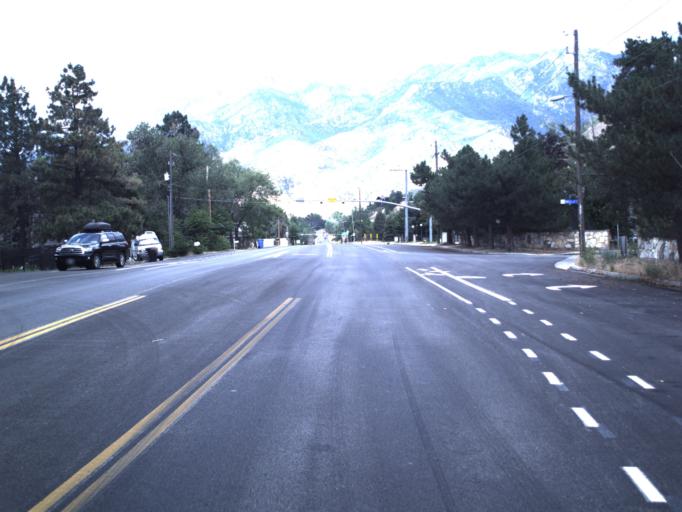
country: US
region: Utah
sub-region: Salt Lake County
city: Cottonwood Heights
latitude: 40.5991
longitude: -111.7977
